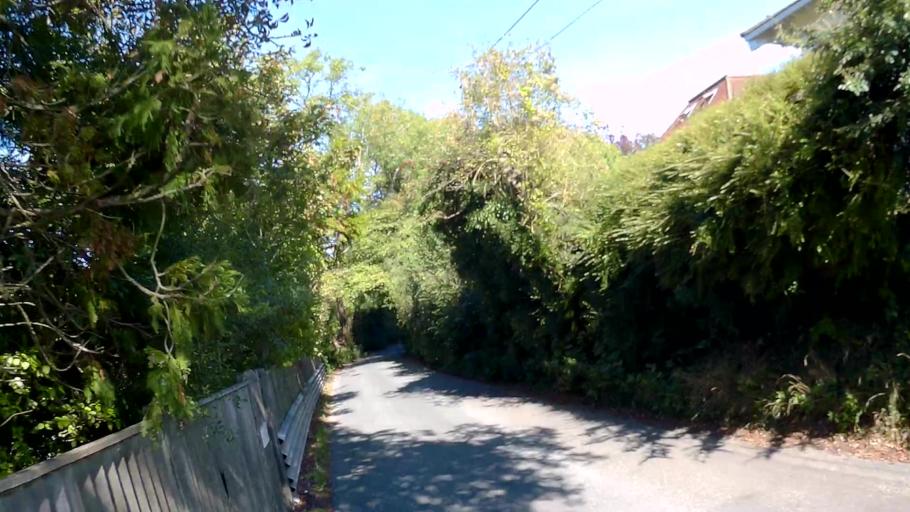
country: GB
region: England
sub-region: Hampshire
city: Andover
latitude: 51.1534
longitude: -1.4474
